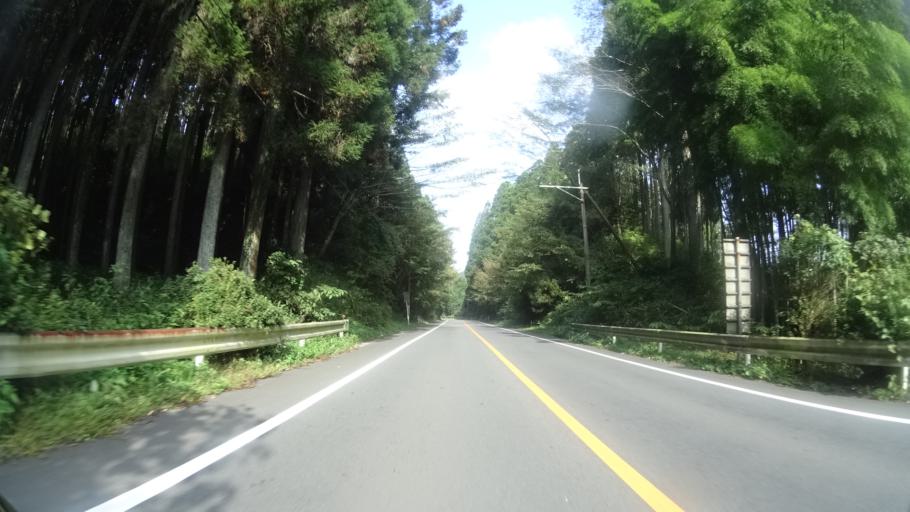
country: JP
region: Kumamoto
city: Aso
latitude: 33.0829
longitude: 131.0639
